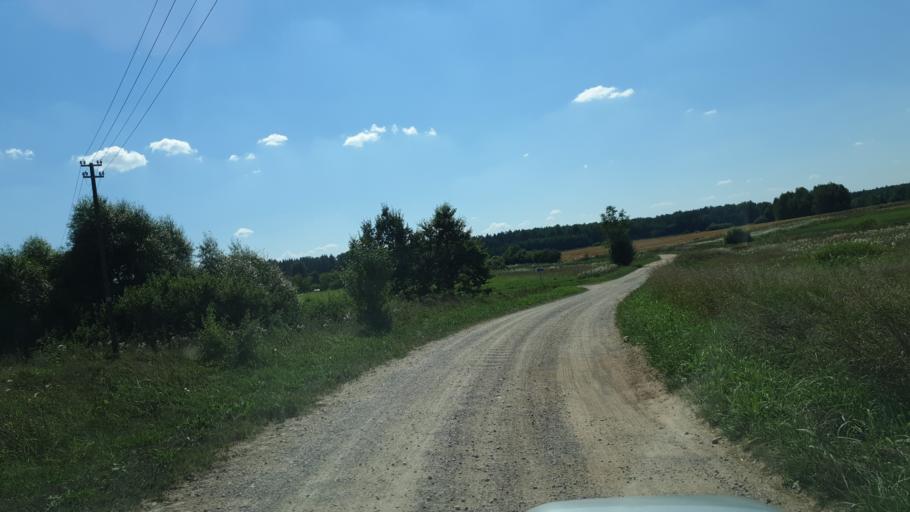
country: LT
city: Sirvintos
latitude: 54.9043
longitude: 24.9107
